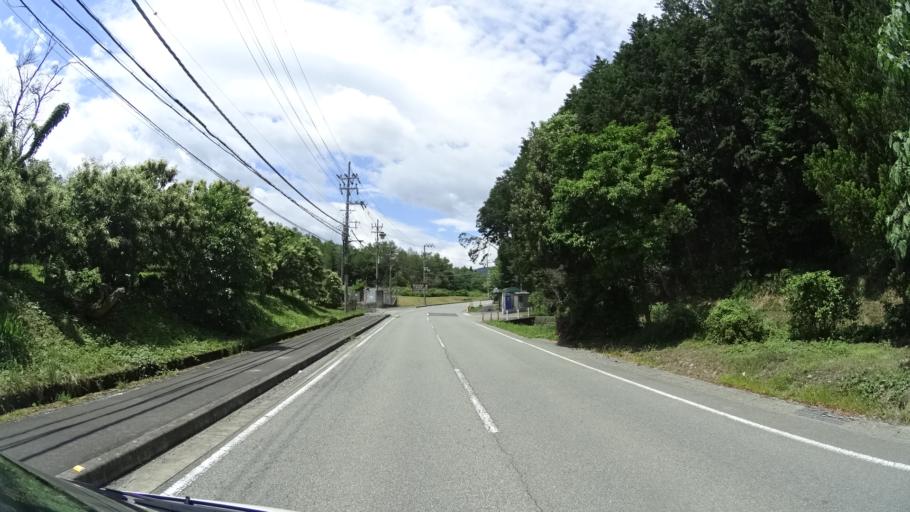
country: JP
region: Kyoto
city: Kameoka
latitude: 35.0199
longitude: 135.5016
